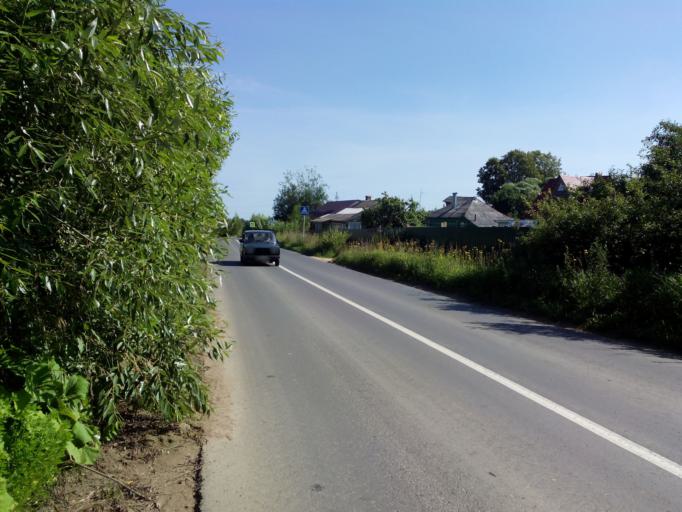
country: RU
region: Moskovskaya
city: Verbilki
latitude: 56.5443
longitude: 37.6154
